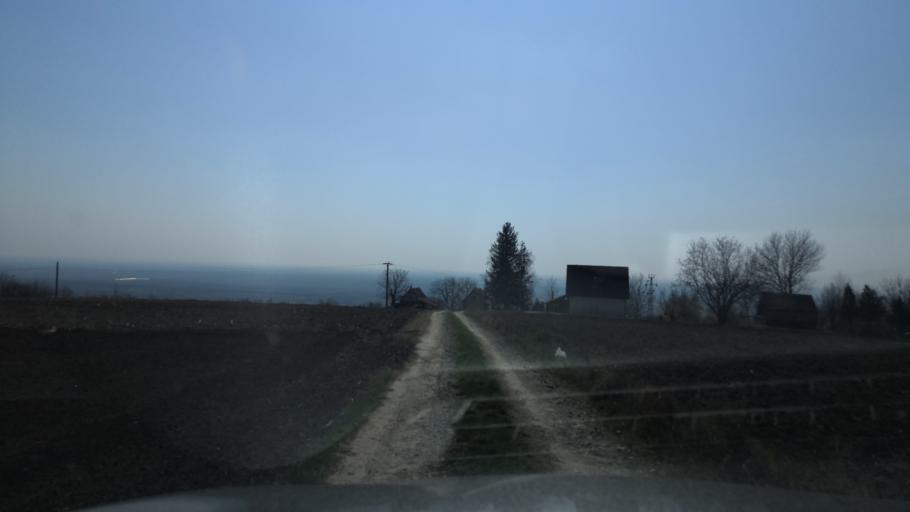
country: RS
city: Krcedin
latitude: 45.1628
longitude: 20.1867
